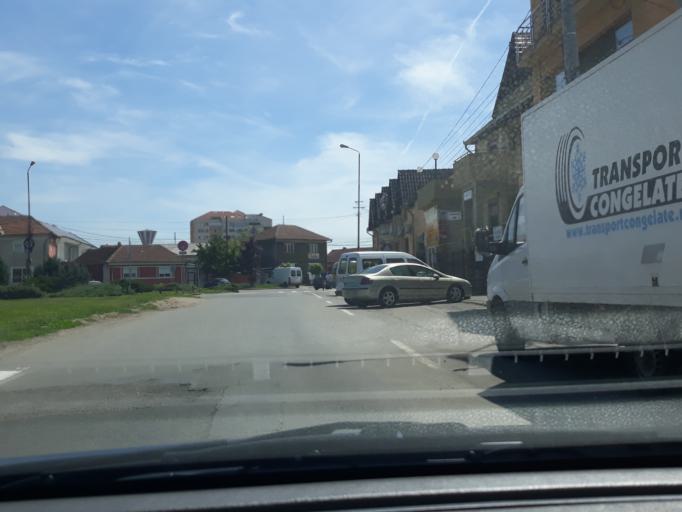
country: RO
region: Bihor
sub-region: Comuna Biharea
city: Oradea
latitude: 47.0646
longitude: 21.9043
